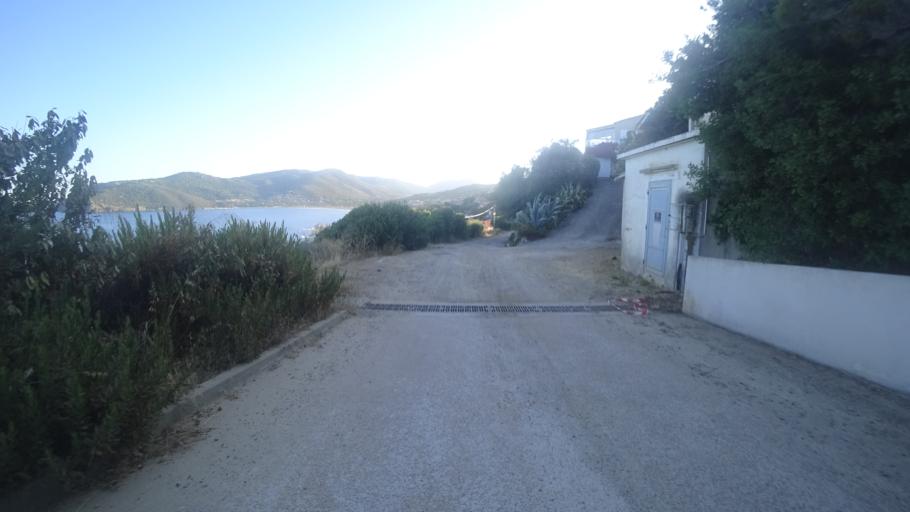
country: FR
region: Corsica
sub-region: Departement de la Corse-du-Sud
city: Alata
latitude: 41.9761
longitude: 8.6638
